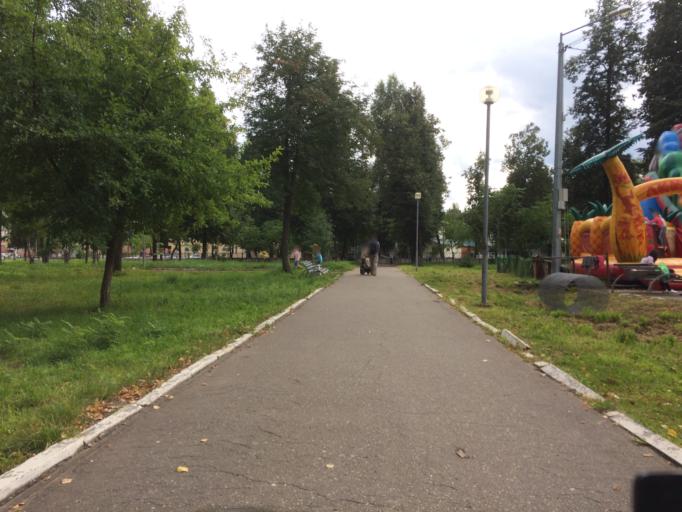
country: RU
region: Mariy-El
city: Yoshkar-Ola
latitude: 56.6394
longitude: 47.8671
